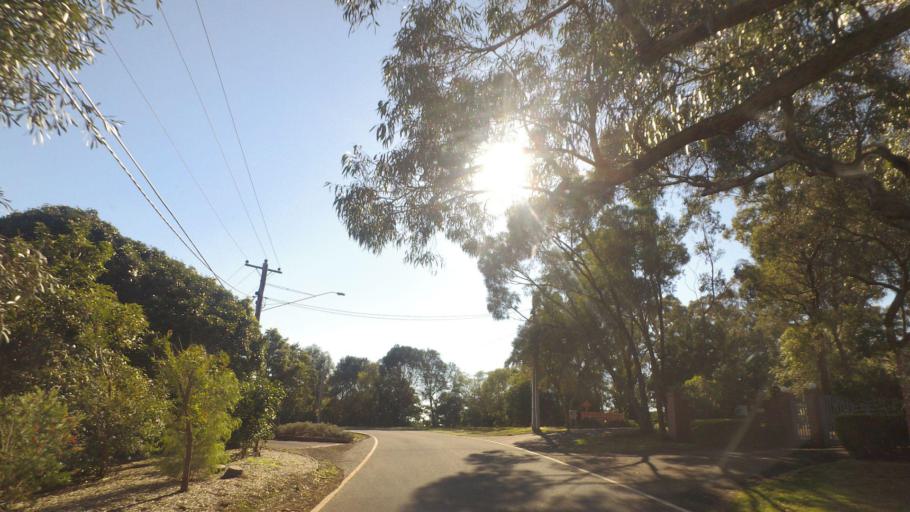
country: AU
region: Victoria
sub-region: Nillumbik
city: Eltham
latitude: -37.7491
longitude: 145.1503
